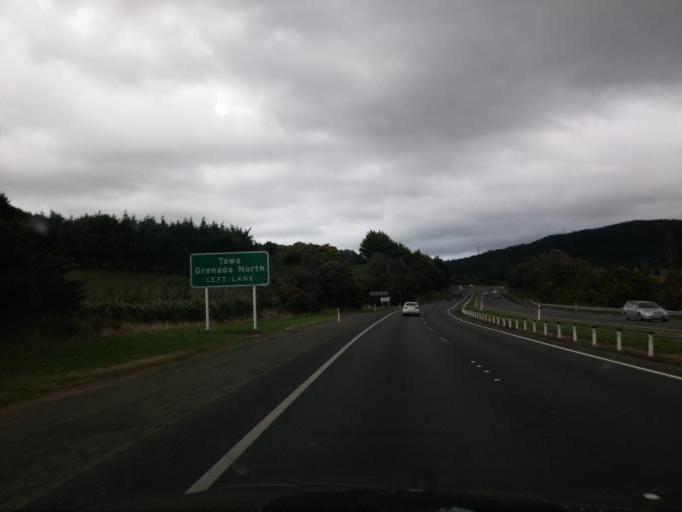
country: NZ
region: Wellington
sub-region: Porirua City
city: Porirua
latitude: -41.1763
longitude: 174.8302
